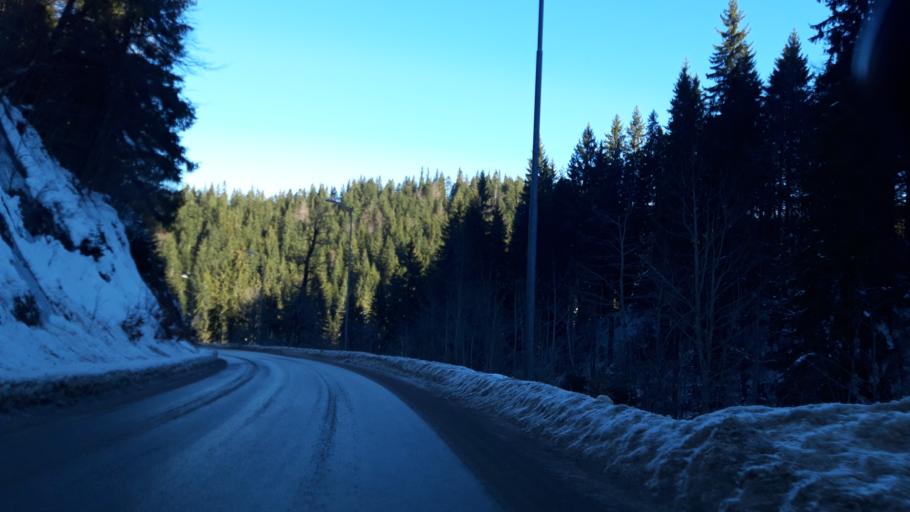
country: BA
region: Republika Srpska
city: Koran
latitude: 43.7404
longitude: 18.5688
